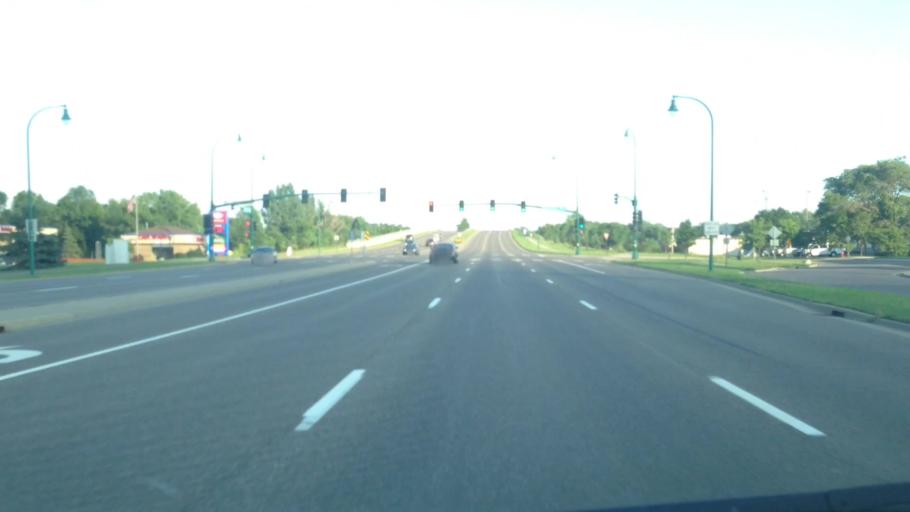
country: US
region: Minnesota
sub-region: Hennepin County
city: Crystal
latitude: 45.0520
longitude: -93.3558
